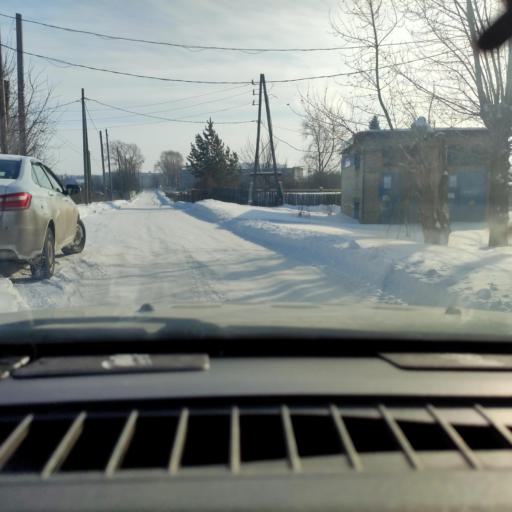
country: RU
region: Perm
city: Gamovo
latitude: 57.8755
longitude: 56.0854
